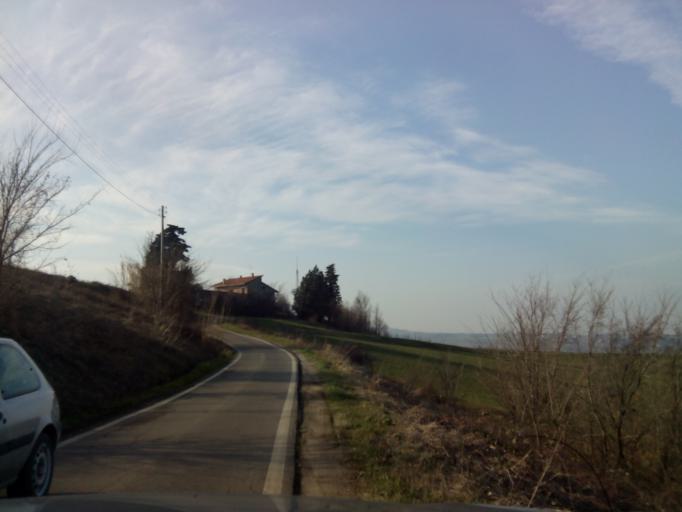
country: IT
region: Emilia-Romagna
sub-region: Provincia di Ravenna
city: Riolo Terme
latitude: 44.3108
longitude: 11.6863
